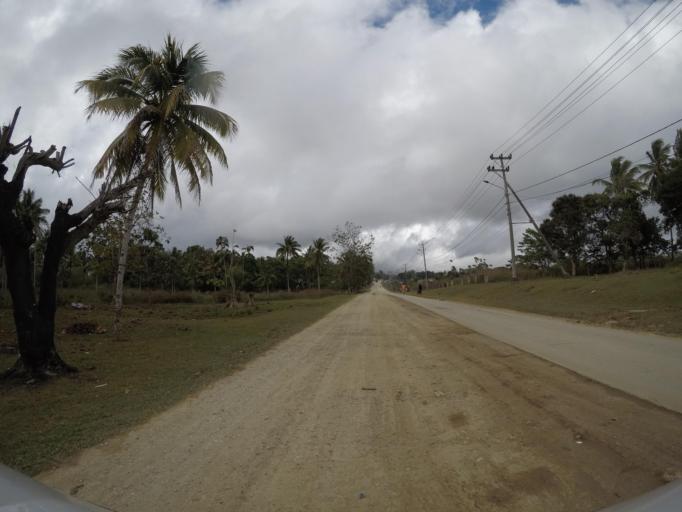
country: TL
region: Lautem
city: Lospalos
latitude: -8.5045
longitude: 126.9890
